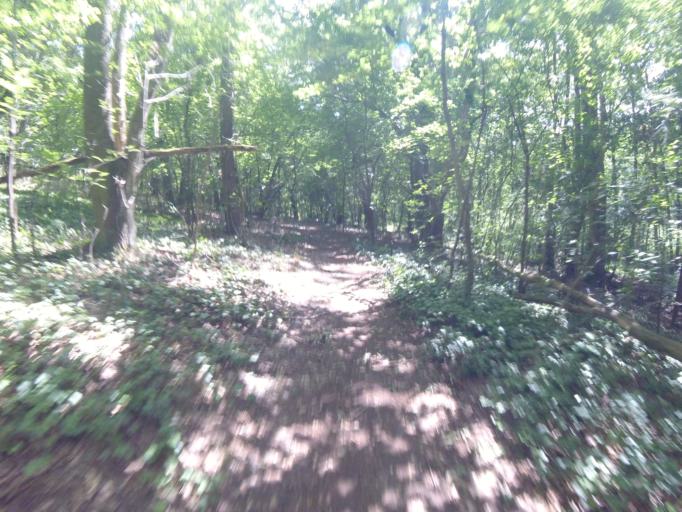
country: DE
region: Brandenburg
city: Bestensee
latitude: 52.2568
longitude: 13.6068
